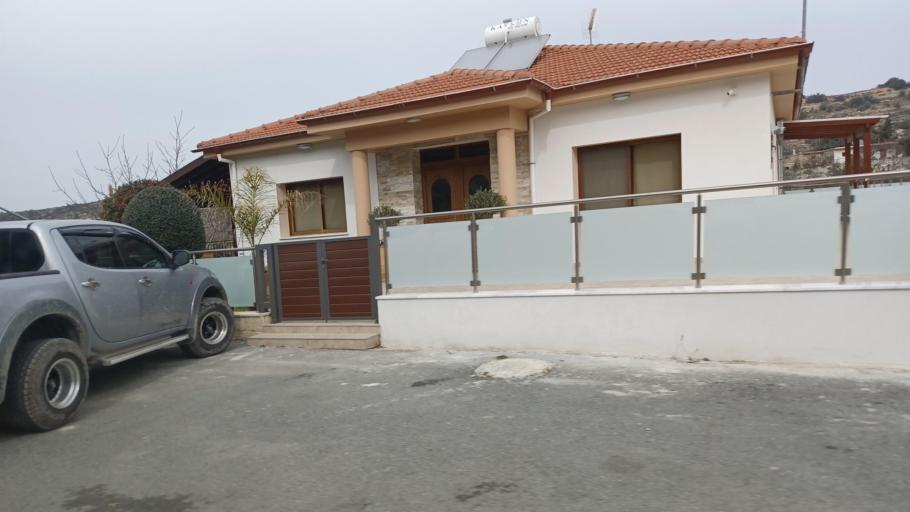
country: CY
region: Limassol
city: Pachna
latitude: 34.7776
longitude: 32.7895
